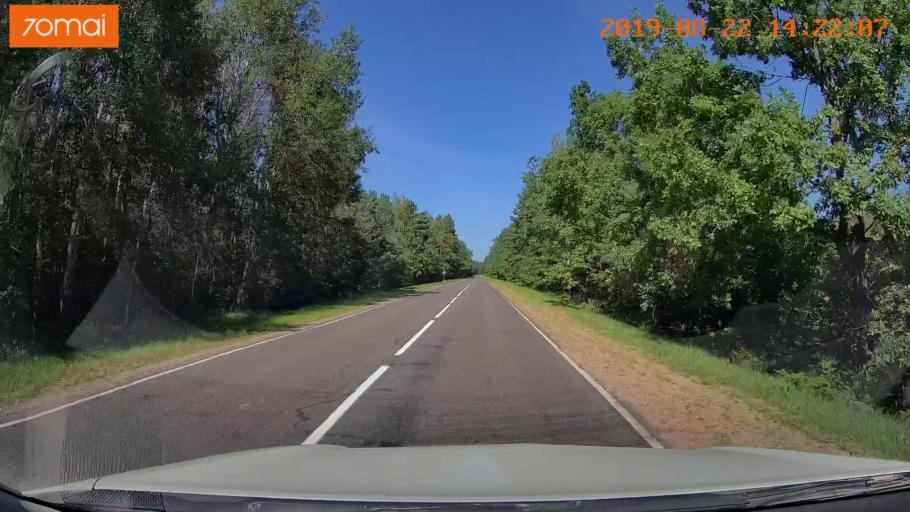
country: BY
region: Mogilev
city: Asipovichy
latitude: 53.2723
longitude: 28.5681
